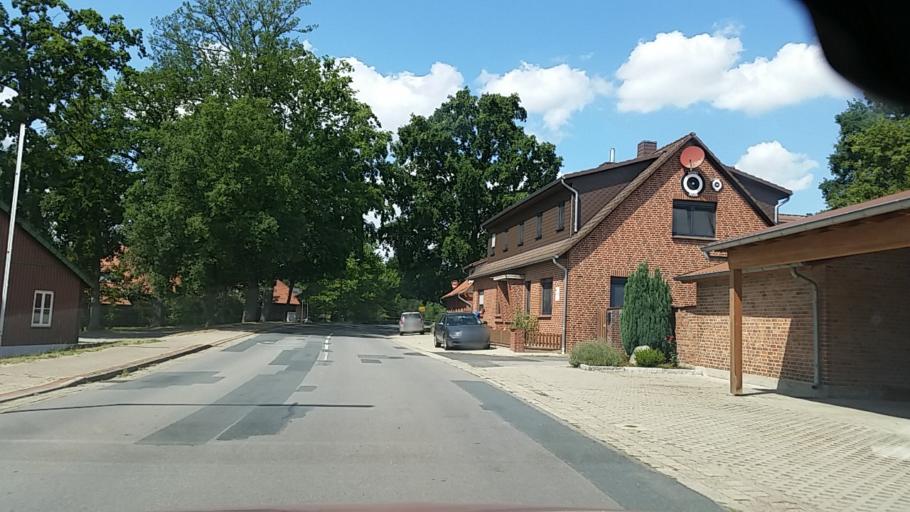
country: DE
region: Lower Saxony
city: Hankensbuttel
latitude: 52.7192
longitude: 10.6199
